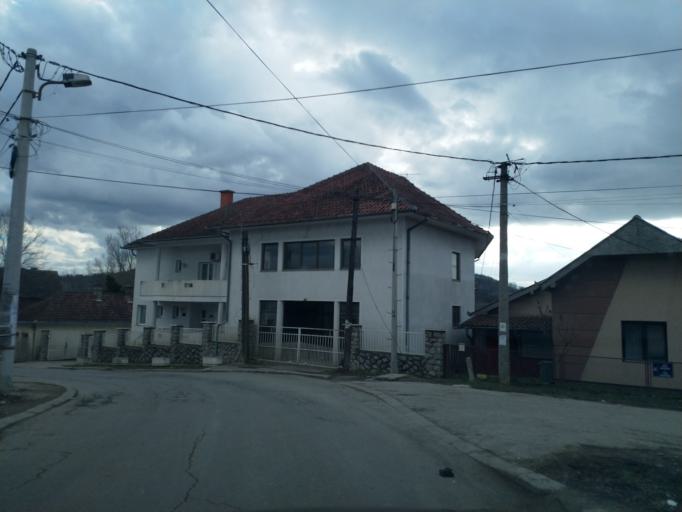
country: RS
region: Central Serbia
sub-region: Belgrade
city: Grocka
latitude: 44.5801
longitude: 20.7381
